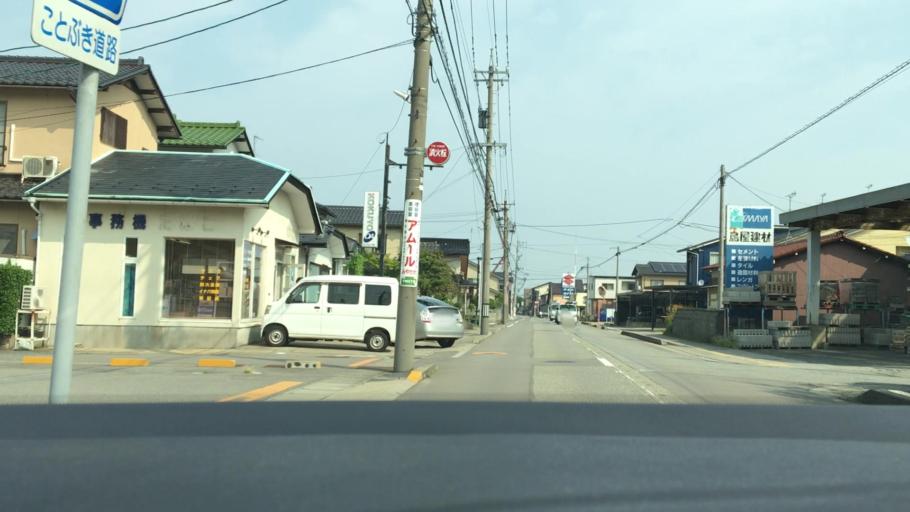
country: JP
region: Ishikawa
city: Nonoichi
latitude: 36.5236
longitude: 136.6042
